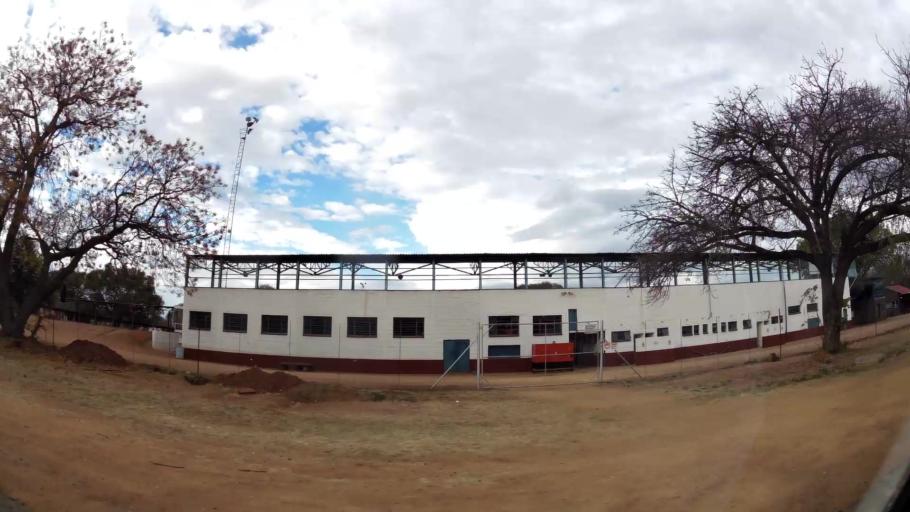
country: ZA
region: Limpopo
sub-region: Waterberg District Municipality
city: Modimolle
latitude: -24.5132
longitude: 28.7062
